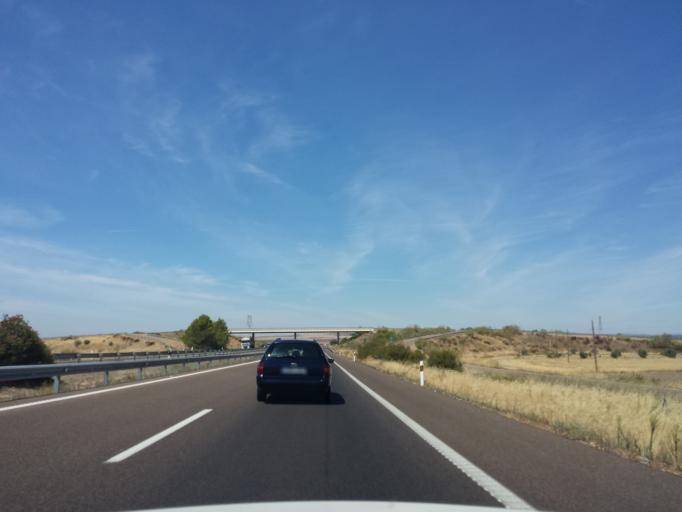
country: ES
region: Extremadura
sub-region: Provincia de Badajoz
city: San Pedro de Merida
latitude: 38.9500
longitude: -6.2164
